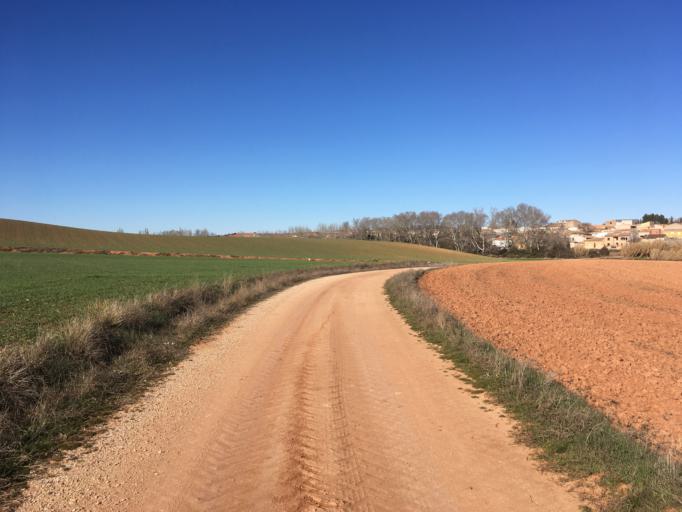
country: ES
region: Castille-La Mancha
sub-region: Provincia de Cuenca
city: Atalaya del Canavate
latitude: 39.5445
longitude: -2.2465
